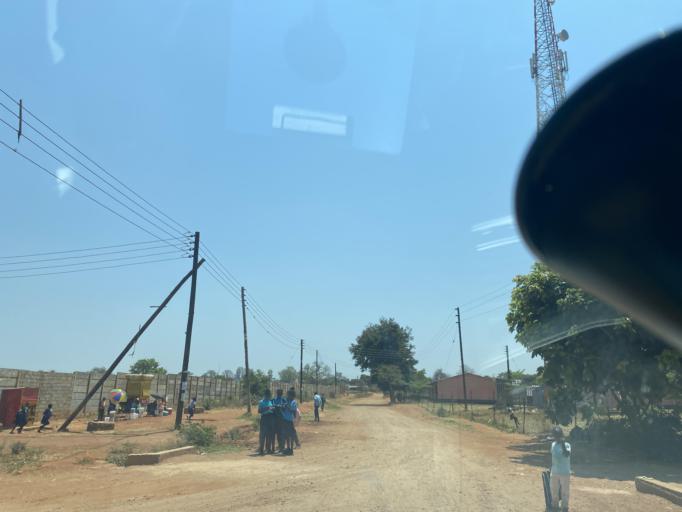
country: ZM
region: Southern
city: Nakambala
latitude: -15.5093
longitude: 27.9281
